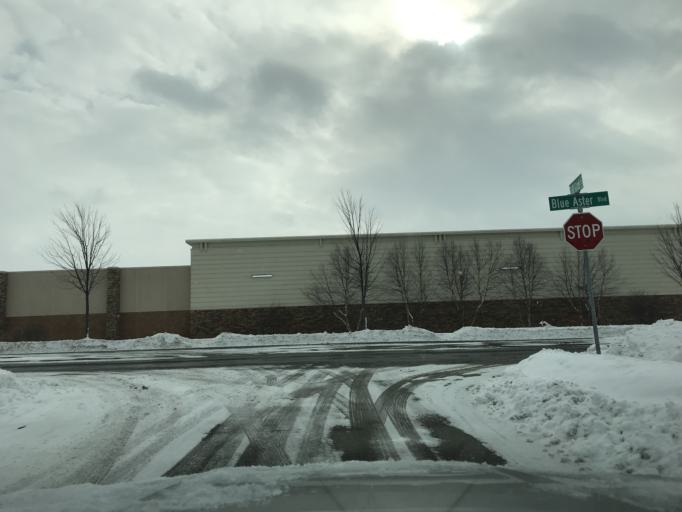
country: US
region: Wisconsin
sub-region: Dane County
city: Sun Prairie
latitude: 43.1720
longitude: -89.2678
